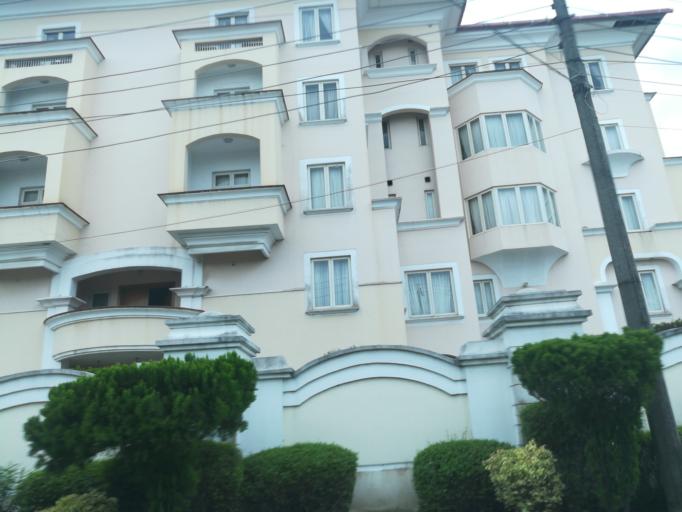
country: NG
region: Lagos
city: Ikoyi
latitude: 6.4474
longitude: 3.4584
